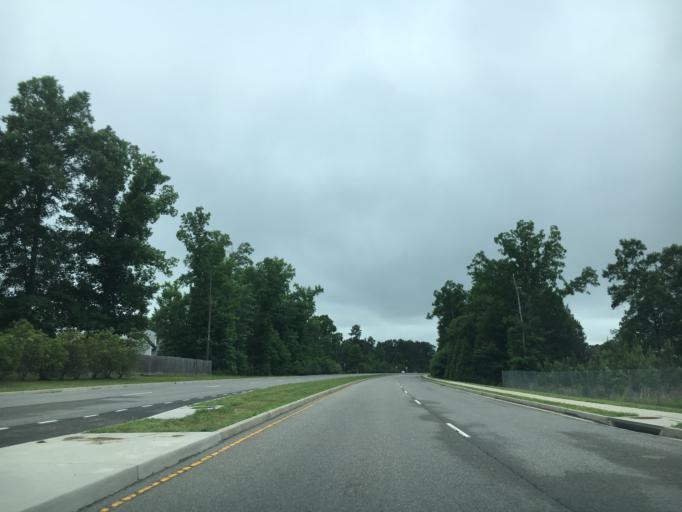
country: US
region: Virginia
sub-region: Henrico County
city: Short Pump
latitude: 37.6295
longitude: -77.6149
